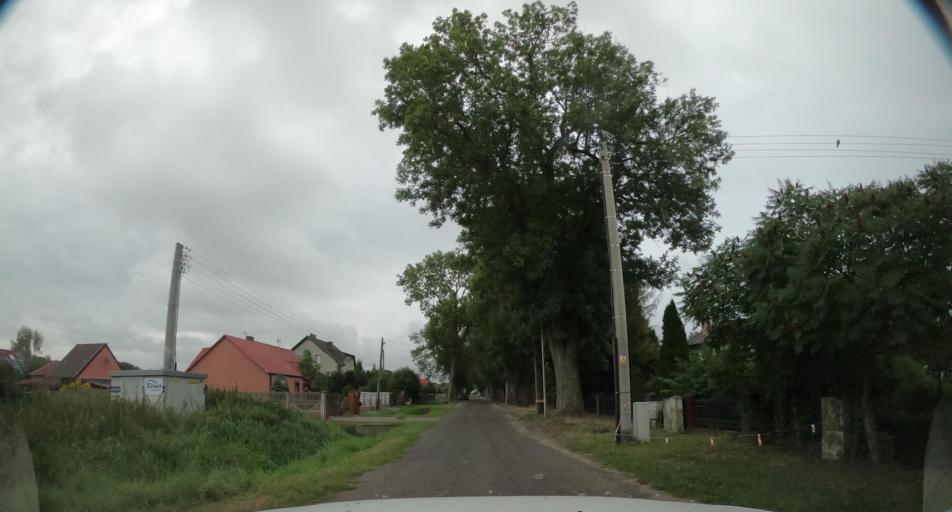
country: PL
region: West Pomeranian Voivodeship
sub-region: Powiat stargardzki
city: Stargard Szczecinski
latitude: 53.3337
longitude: 15.0649
